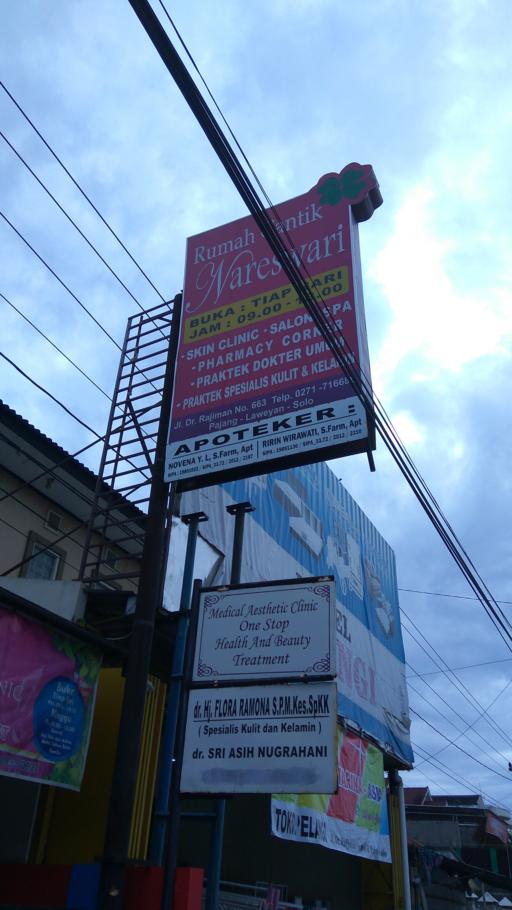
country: ID
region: Central Java
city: Baki
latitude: -7.5682
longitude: 110.7871
